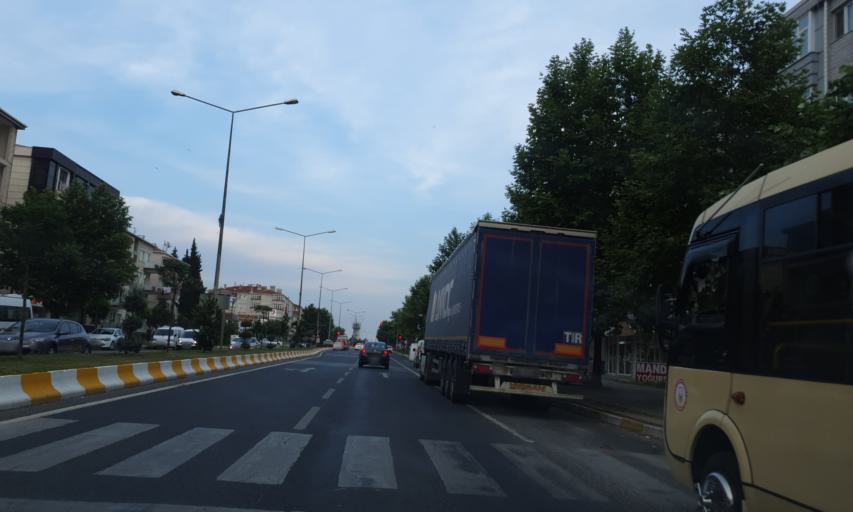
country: TR
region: Kirklareli
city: Luleburgaz
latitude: 41.4018
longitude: 27.3690
